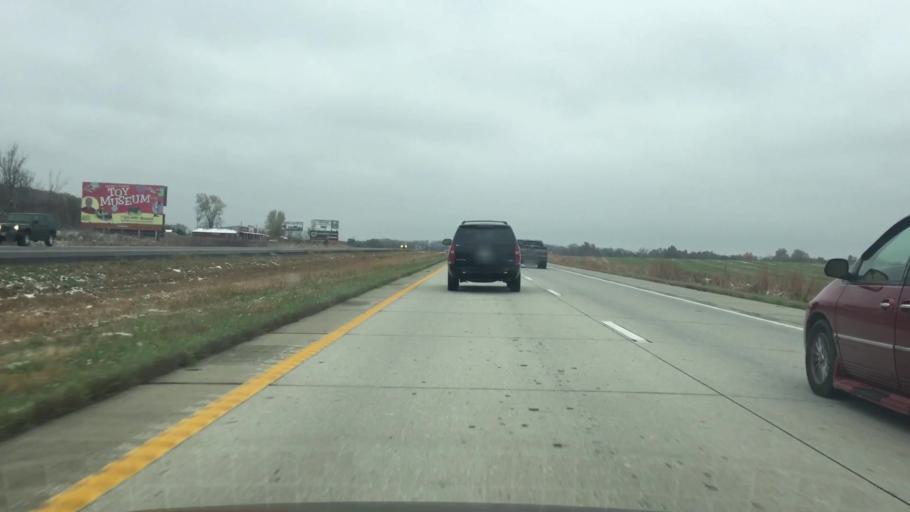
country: US
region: Missouri
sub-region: Saint Clair County
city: Osceola
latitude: 37.9973
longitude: -93.6543
